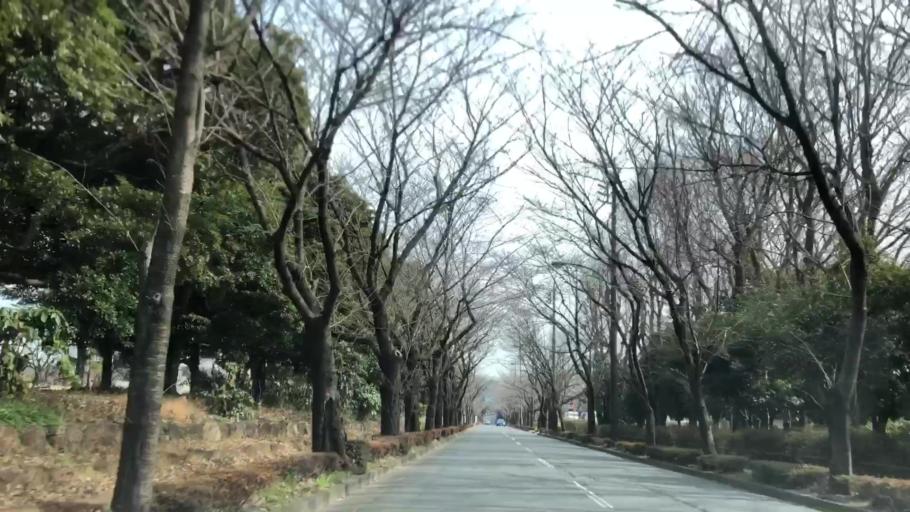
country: JP
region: Saitama
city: Wako
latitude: 35.7762
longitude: 139.5994
